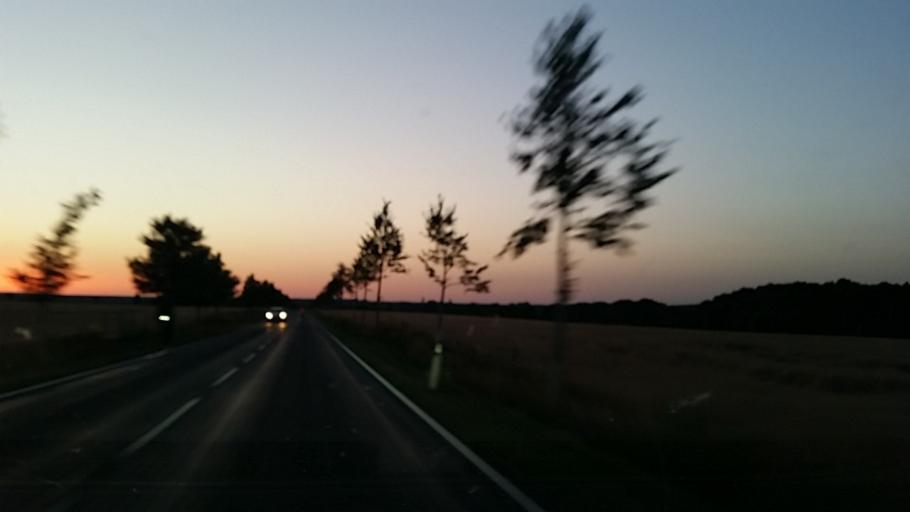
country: DE
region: Brandenburg
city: Niemegk
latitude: 52.0524
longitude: 12.7001
